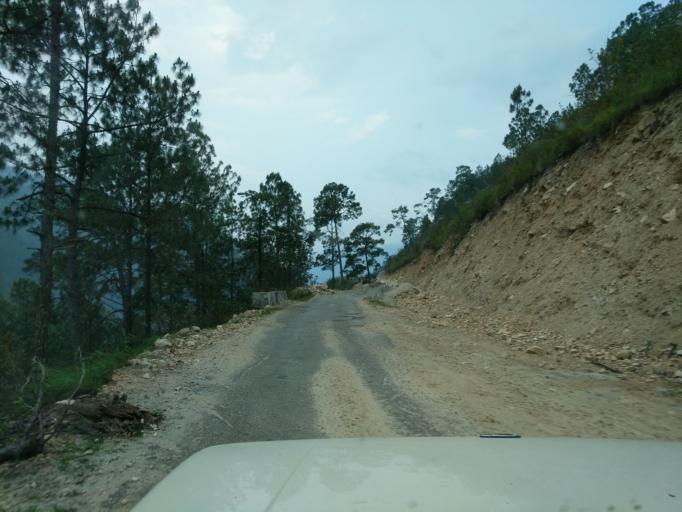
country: BT
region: Mongar
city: Mongar
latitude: 27.2651
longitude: 91.1906
